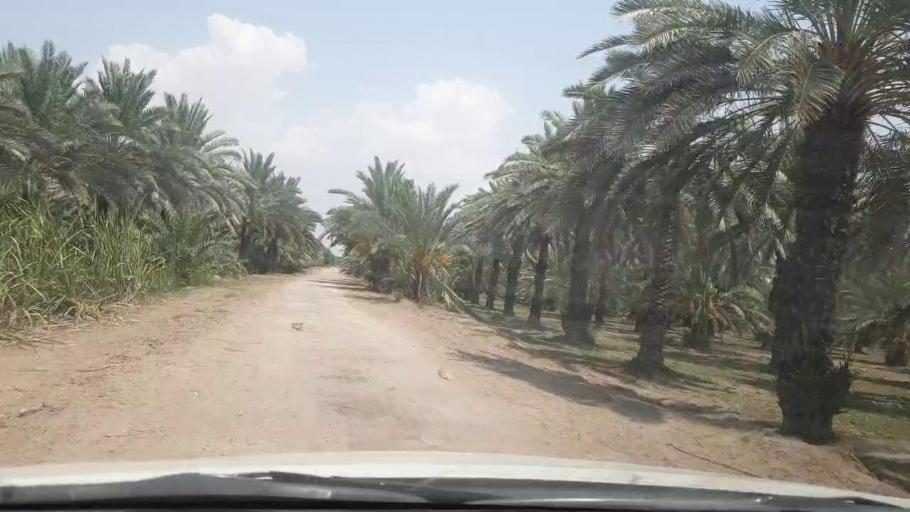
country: PK
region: Sindh
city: Khairpur
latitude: 27.5497
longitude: 68.8351
